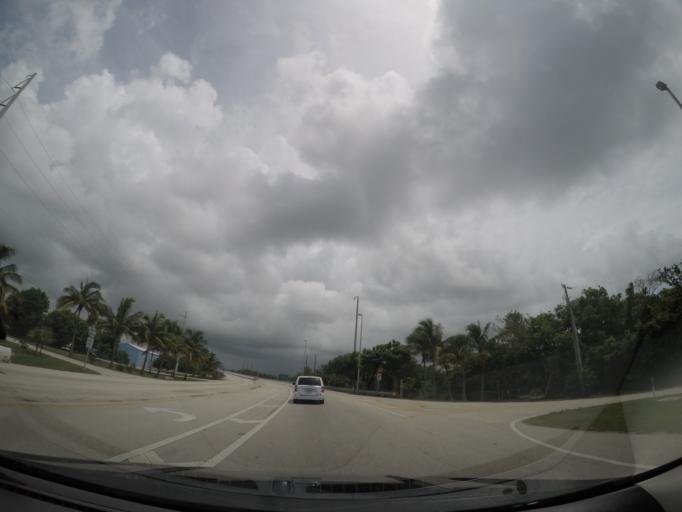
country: US
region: Florida
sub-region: Monroe County
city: North Key Largo
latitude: 25.1733
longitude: -80.3740
